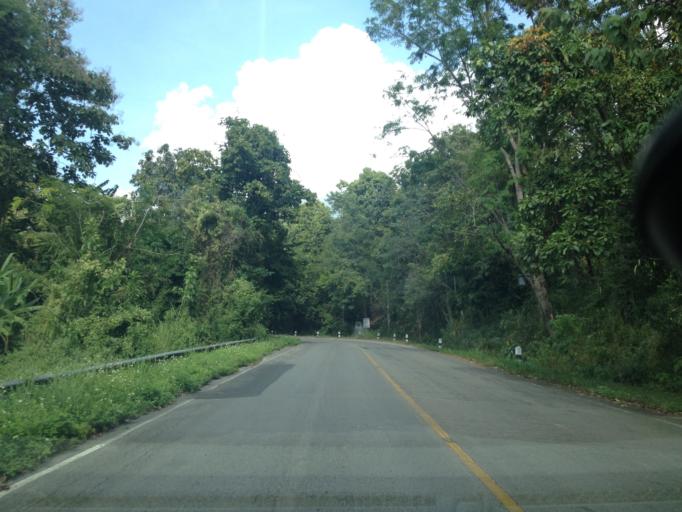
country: TH
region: Chiang Mai
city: Hang Dong
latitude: 18.7803
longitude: 98.8512
